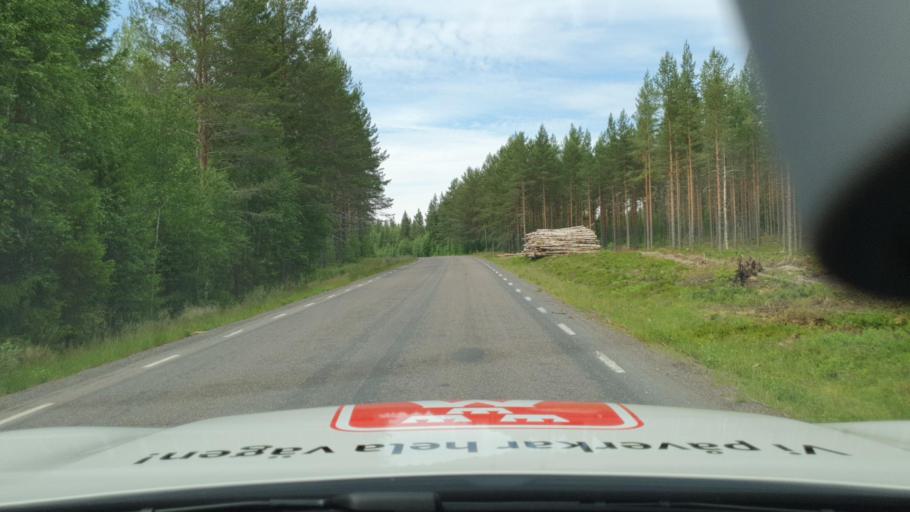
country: NO
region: Hedmark
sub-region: Grue
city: Kirkenaer
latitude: 60.6968
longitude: 12.6219
